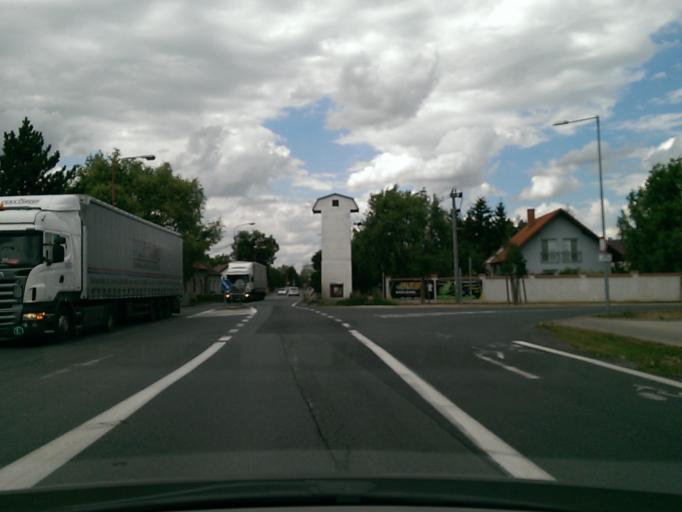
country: CZ
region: Central Bohemia
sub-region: Okres Nymburk
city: Podebrady
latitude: 50.1353
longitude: 15.0970
